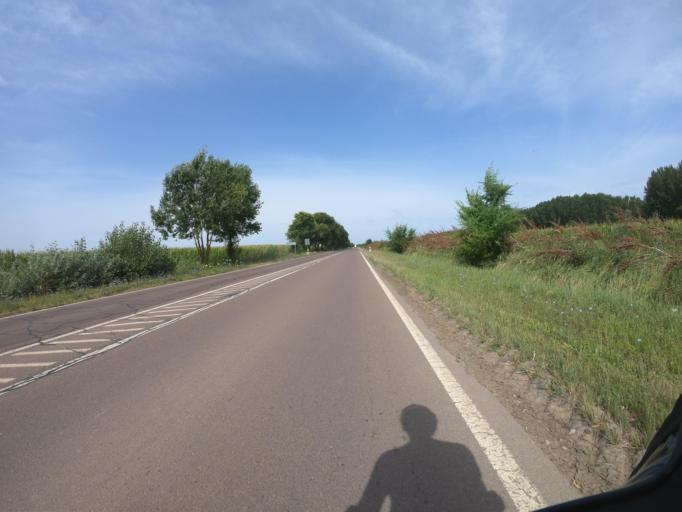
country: HU
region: Jasz-Nagykun-Szolnok
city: Tiszafured
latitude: 47.5985
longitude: 20.8124
